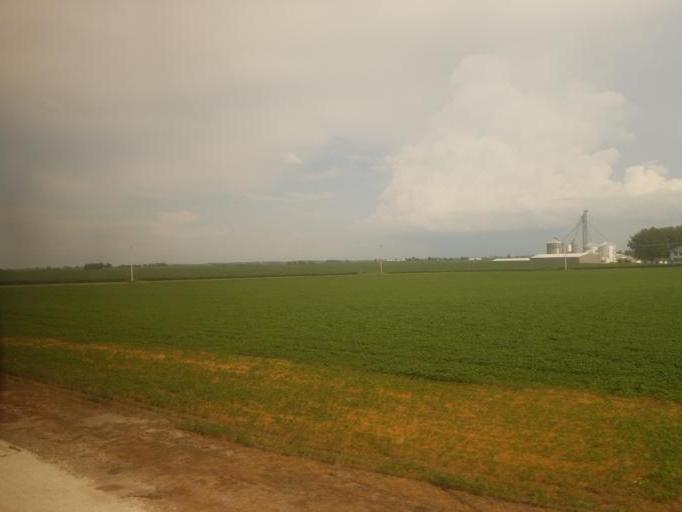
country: US
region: Illinois
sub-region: Henry County
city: Galva
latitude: 41.1248
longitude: -90.1366
